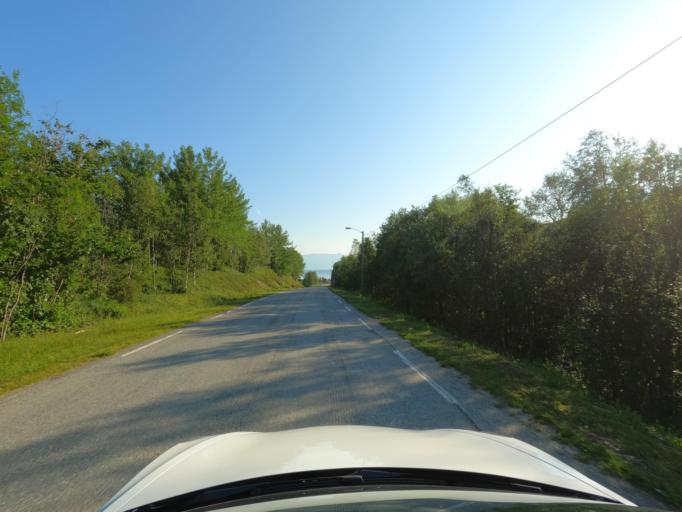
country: NO
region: Nordland
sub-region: Narvik
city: Bjerkvik
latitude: 68.5365
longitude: 17.4837
